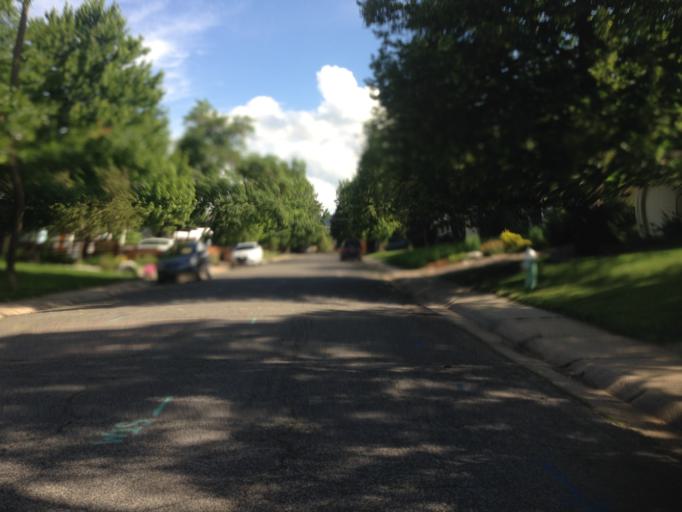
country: US
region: Colorado
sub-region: Boulder County
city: Boulder
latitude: 40.0312
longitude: -105.2752
